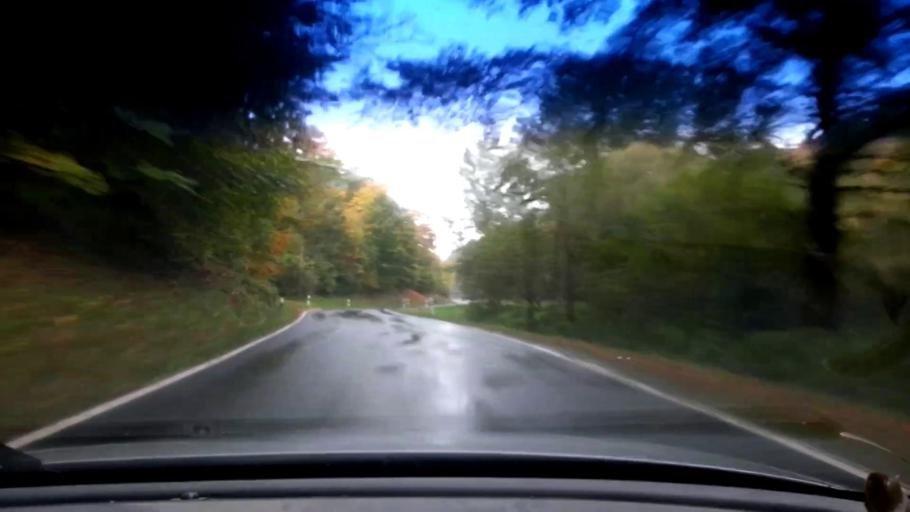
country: DE
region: Bavaria
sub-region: Upper Franconia
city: Stadelhofen
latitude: 50.0327
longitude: 11.2018
